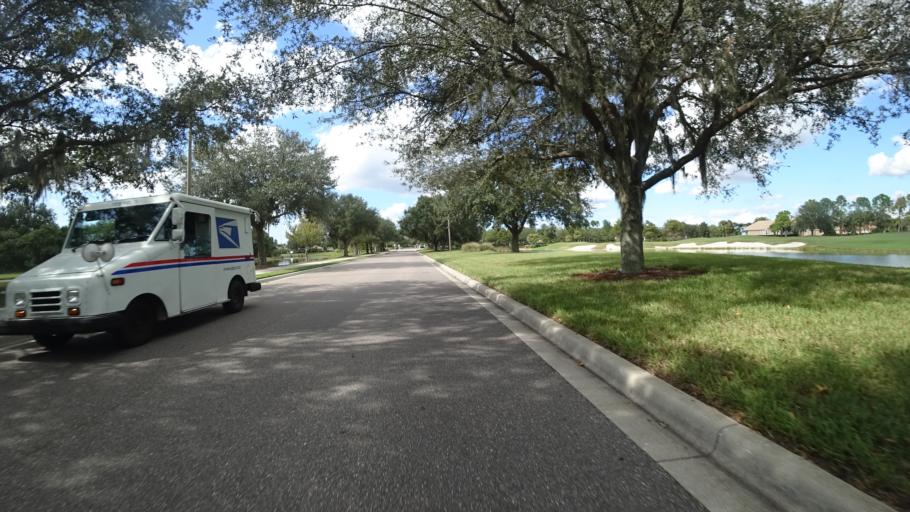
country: US
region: Florida
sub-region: Sarasota County
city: The Meadows
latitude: 27.3962
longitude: -82.4105
